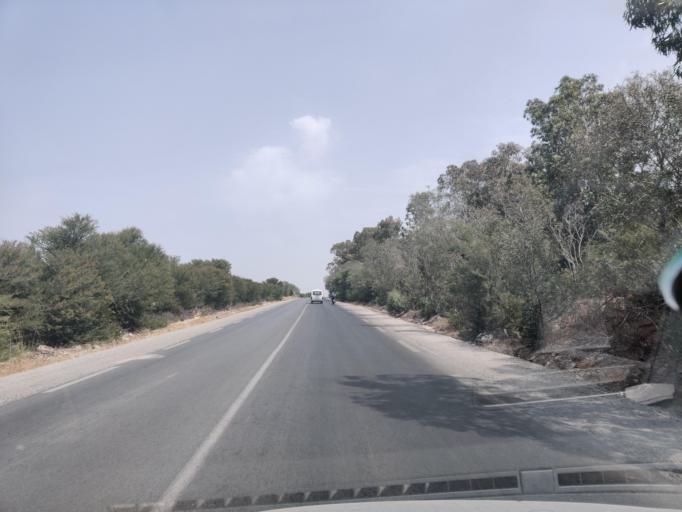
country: TN
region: Nabul
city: Bu `Urqub
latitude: 36.4775
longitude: 10.5721
